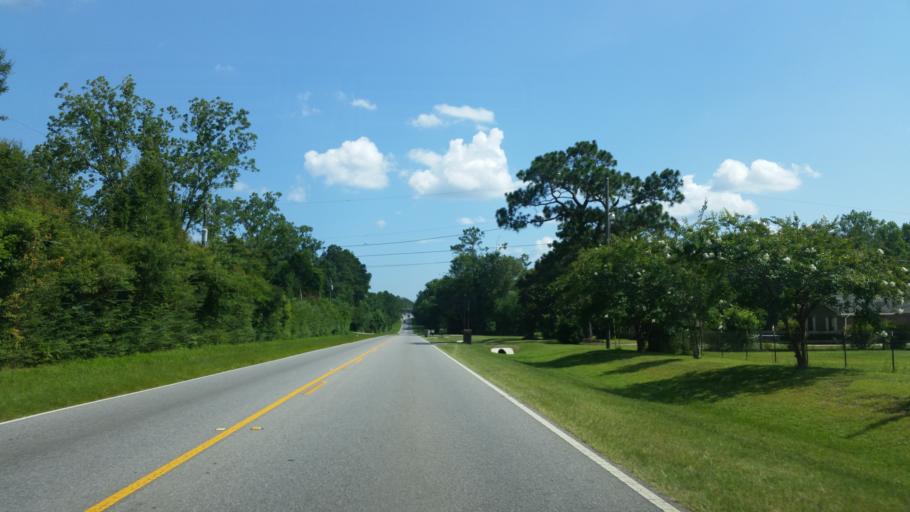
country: US
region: Florida
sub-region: Escambia County
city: Cantonment
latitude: 30.5425
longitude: -87.3804
